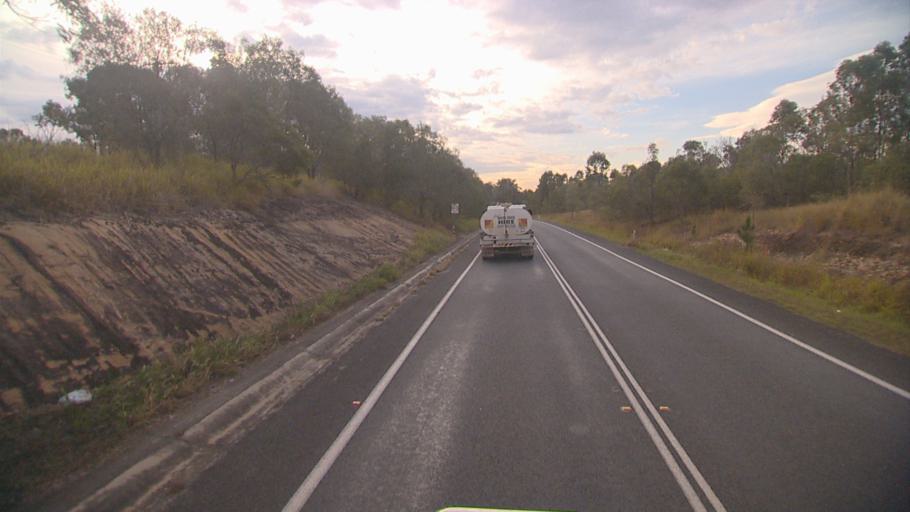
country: AU
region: Queensland
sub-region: Logan
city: Chambers Flat
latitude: -27.8341
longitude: 153.1072
